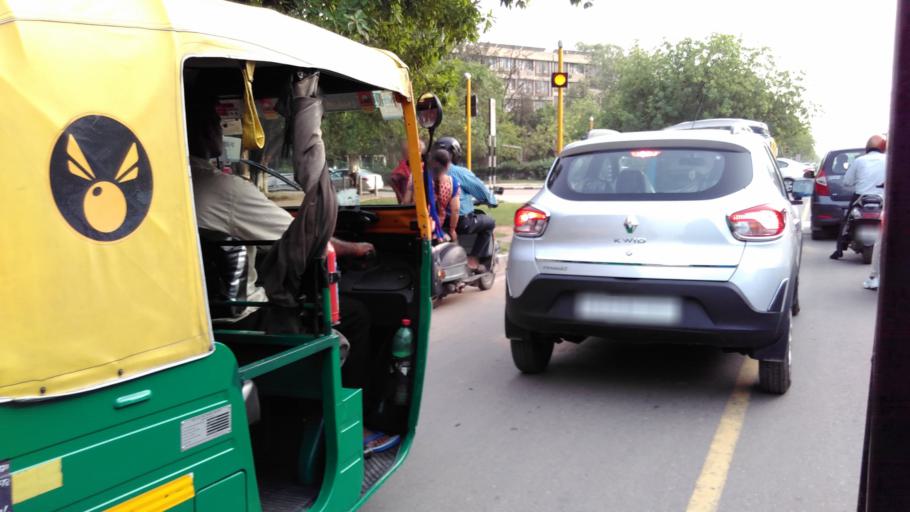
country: IN
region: Chandigarh
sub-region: Chandigarh
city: Chandigarh
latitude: 30.7503
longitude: 76.7917
